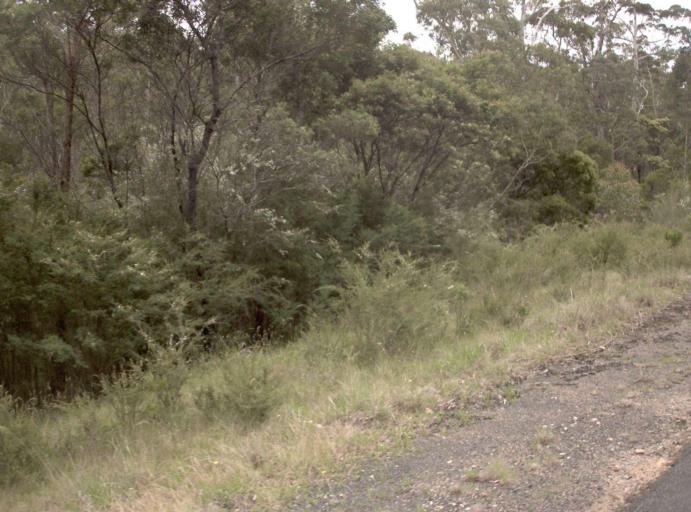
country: AU
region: New South Wales
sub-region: Bombala
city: Bombala
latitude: -37.2640
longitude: 149.2347
